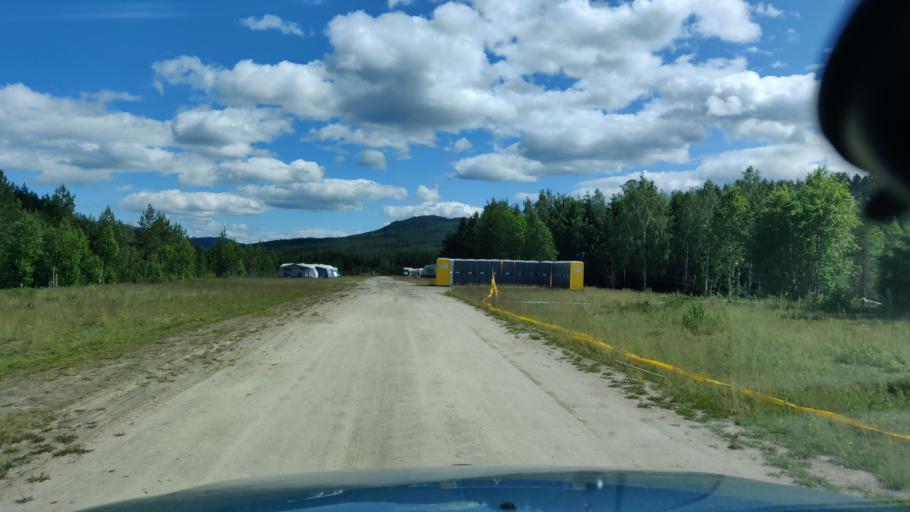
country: NO
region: Hedmark
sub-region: Trysil
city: Innbygda
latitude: 60.9091
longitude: 12.5665
